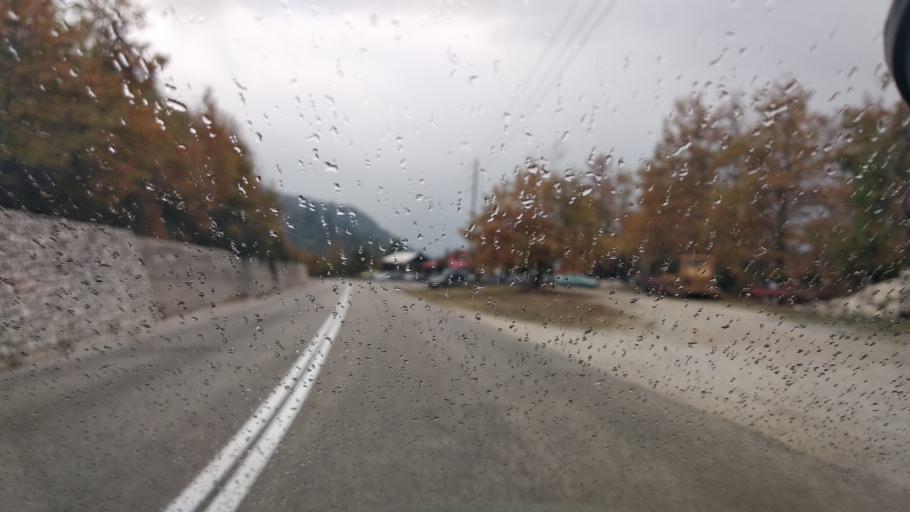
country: GR
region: Thessaly
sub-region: Trikala
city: Pyli
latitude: 39.4939
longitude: 21.5404
